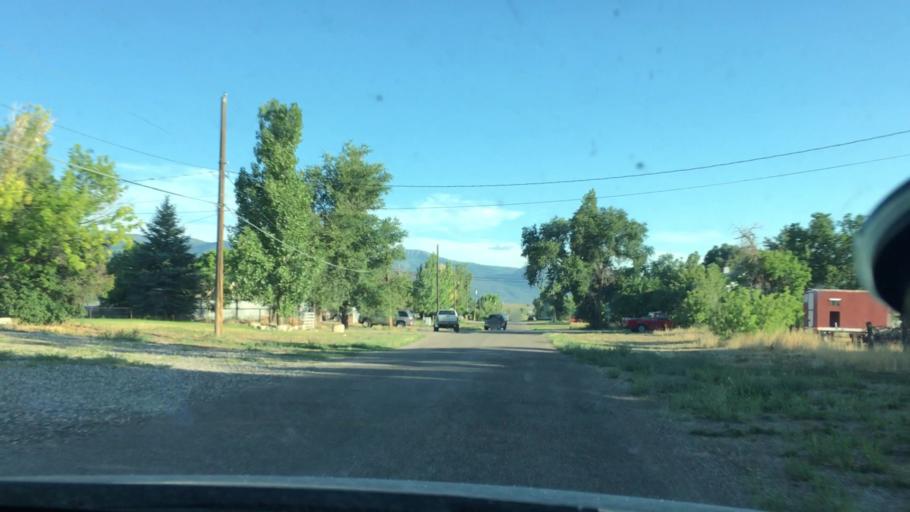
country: US
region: Utah
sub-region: Sanpete County
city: Mount Pleasant
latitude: 39.5436
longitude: -111.4629
